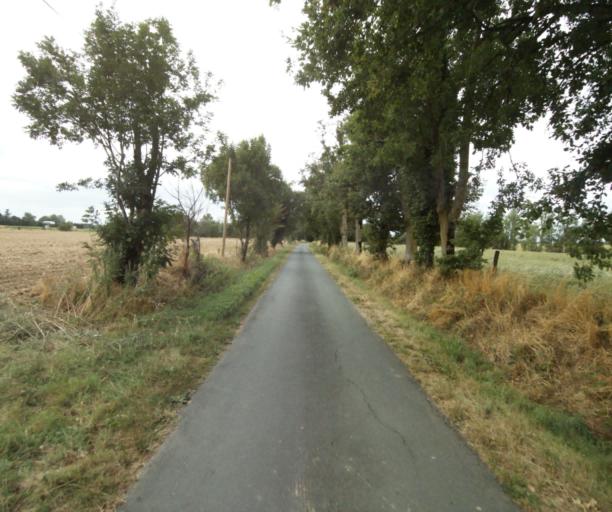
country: FR
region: Midi-Pyrenees
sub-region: Departement du Tarn
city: Soreze
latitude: 43.4614
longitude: 2.0595
